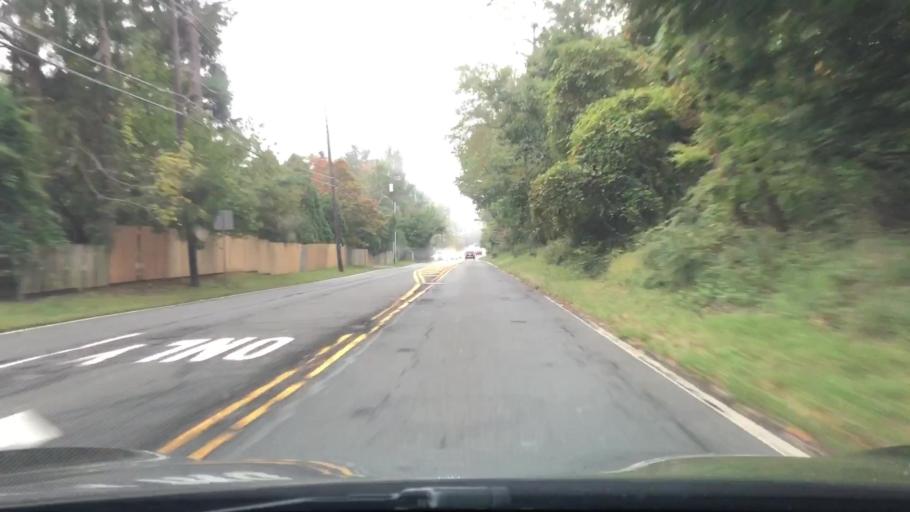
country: US
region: New Jersey
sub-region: Mercer County
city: Lawrenceville
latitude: 40.3213
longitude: -74.6991
